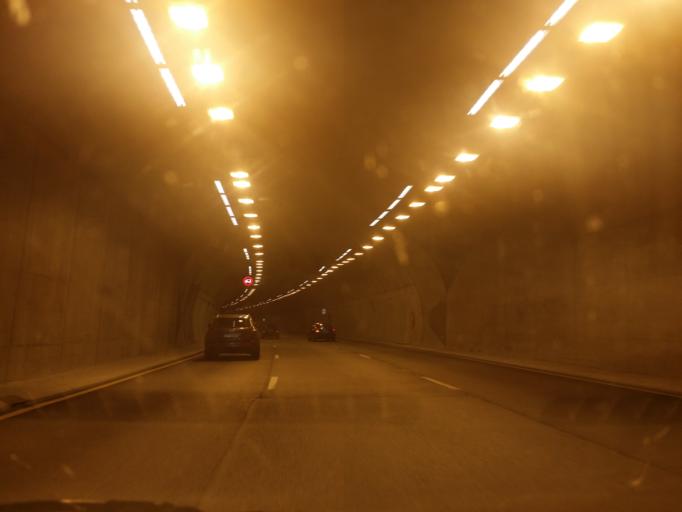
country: NO
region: Oslo
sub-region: Oslo
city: Oslo
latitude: 59.9360
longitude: 10.7891
